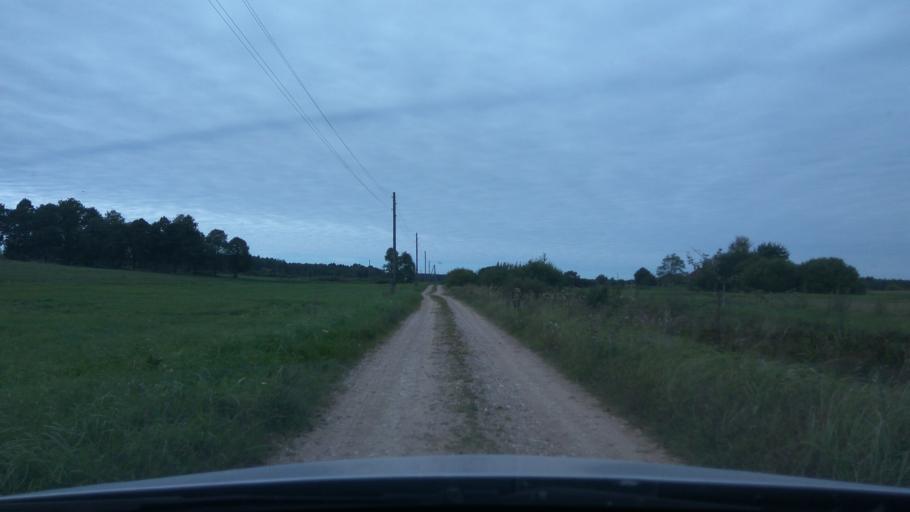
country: LV
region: Kuldigas Rajons
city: Kuldiga
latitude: 57.2418
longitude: 21.9536
